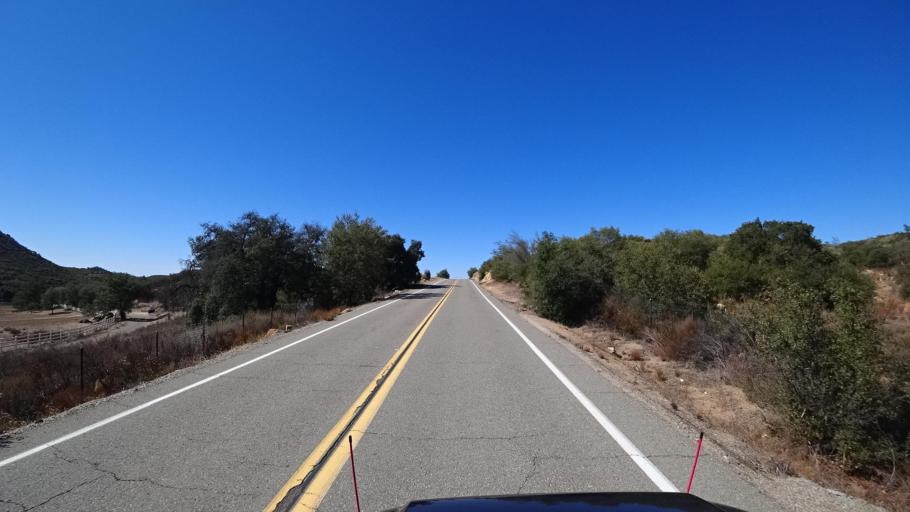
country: US
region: California
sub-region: San Diego County
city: Descanso
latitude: 32.7985
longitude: -116.6524
